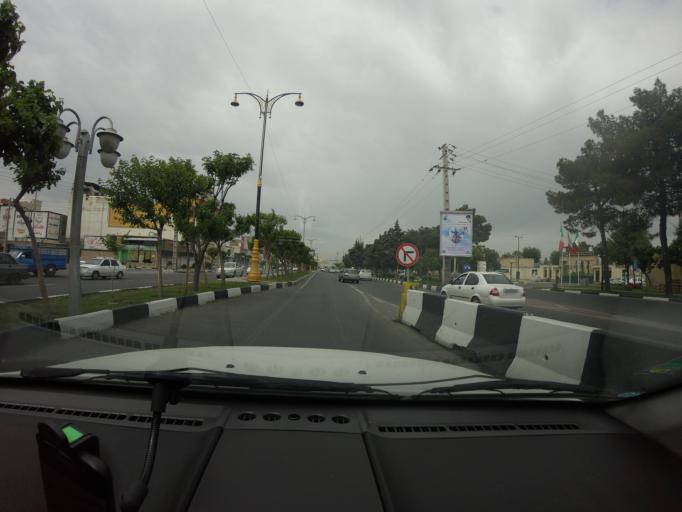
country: IR
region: Tehran
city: Eslamshahr
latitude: 35.5593
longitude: 51.2489
